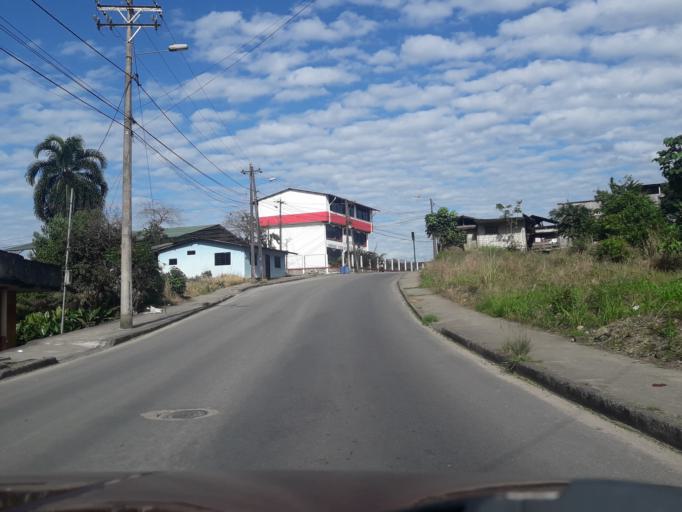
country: EC
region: Napo
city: Tena
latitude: -0.9865
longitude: -77.8262
